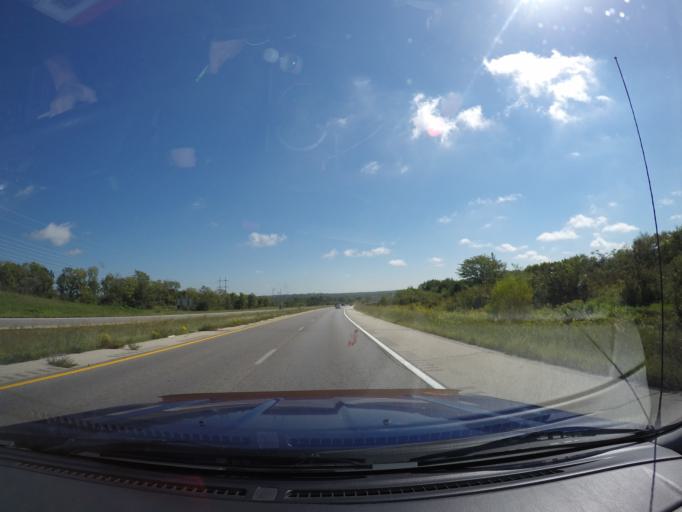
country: US
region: Kansas
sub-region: Johnson County
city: De Soto
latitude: 38.9601
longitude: -94.9350
